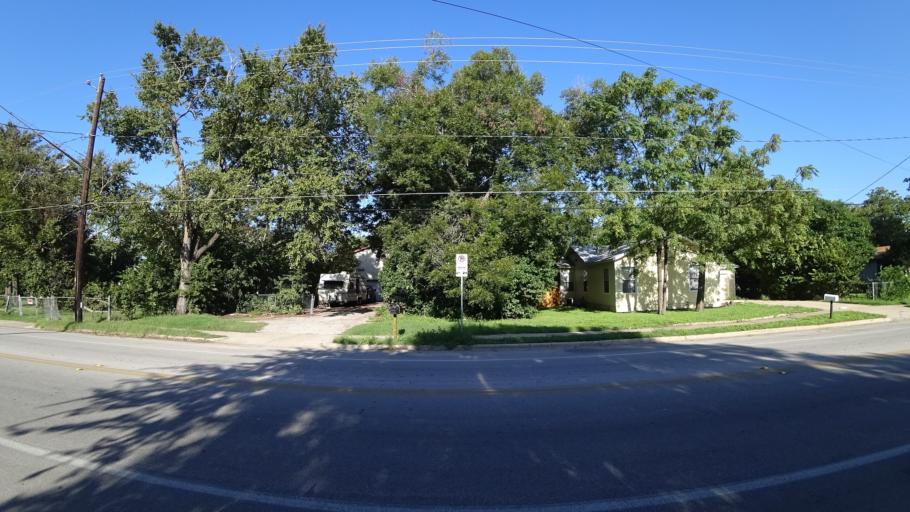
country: US
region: Texas
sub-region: Travis County
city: Wells Branch
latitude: 30.3588
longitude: -97.6947
